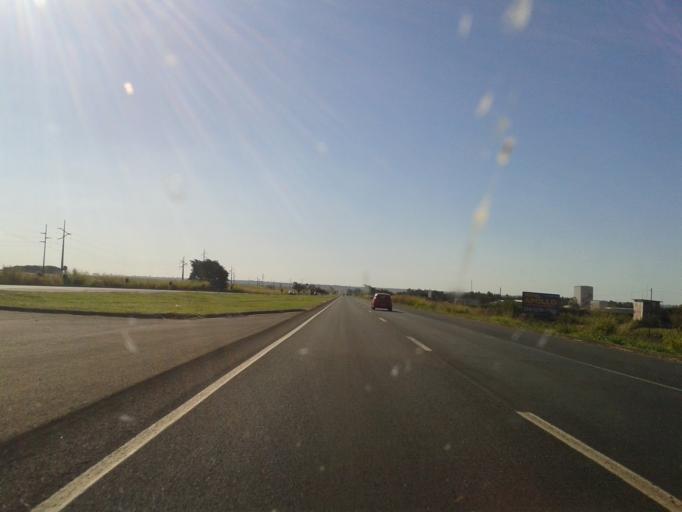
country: BR
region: Minas Gerais
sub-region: Uberlandia
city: Uberlandia
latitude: -19.0447
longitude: -48.1980
